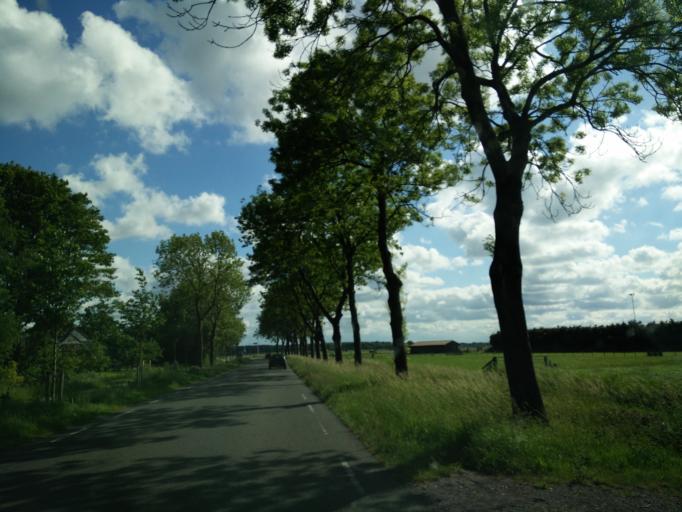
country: NL
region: Groningen
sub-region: Gemeente Groningen
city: Korrewegwijk
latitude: 53.2629
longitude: 6.5891
